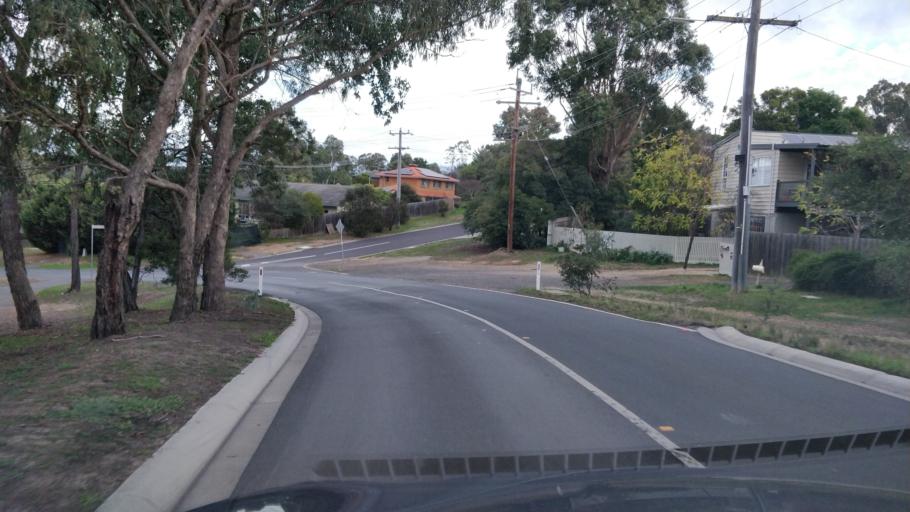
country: AU
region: Victoria
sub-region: Nillumbik
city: Research
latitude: -37.6990
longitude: 145.1814
